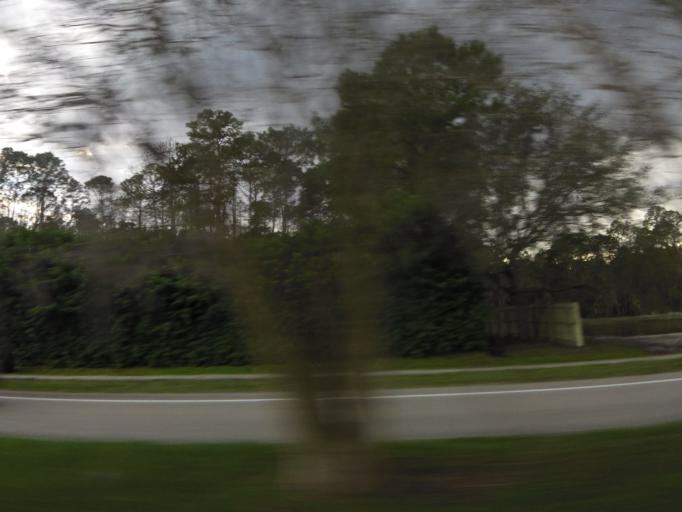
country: US
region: Florida
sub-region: Saint Johns County
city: Fruit Cove
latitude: 30.1760
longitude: -81.5686
